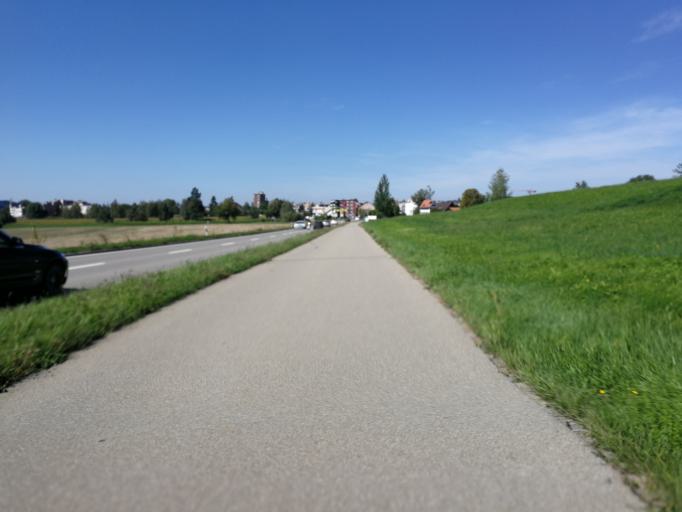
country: CH
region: Zurich
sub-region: Bezirk Hinwil
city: Wetzikon / Kempten
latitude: 47.3256
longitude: 8.8183
